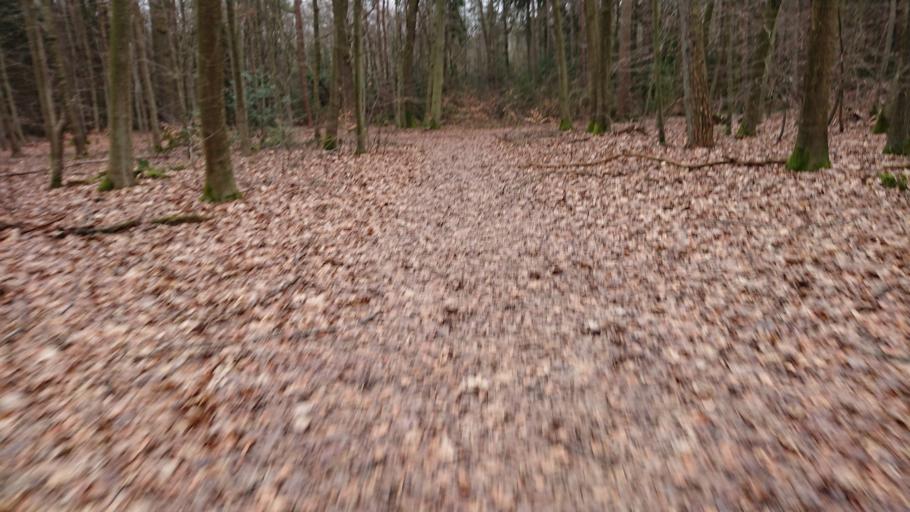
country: DE
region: North Rhine-Westphalia
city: Opladen
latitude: 51.0111
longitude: 7.0535
